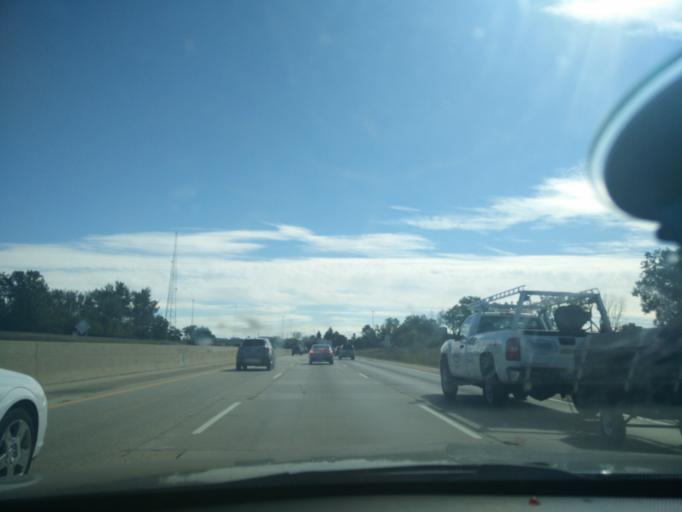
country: US
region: Michigan
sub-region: Oakland County
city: Bingham Farms
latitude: 42.4924
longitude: -83.2894
